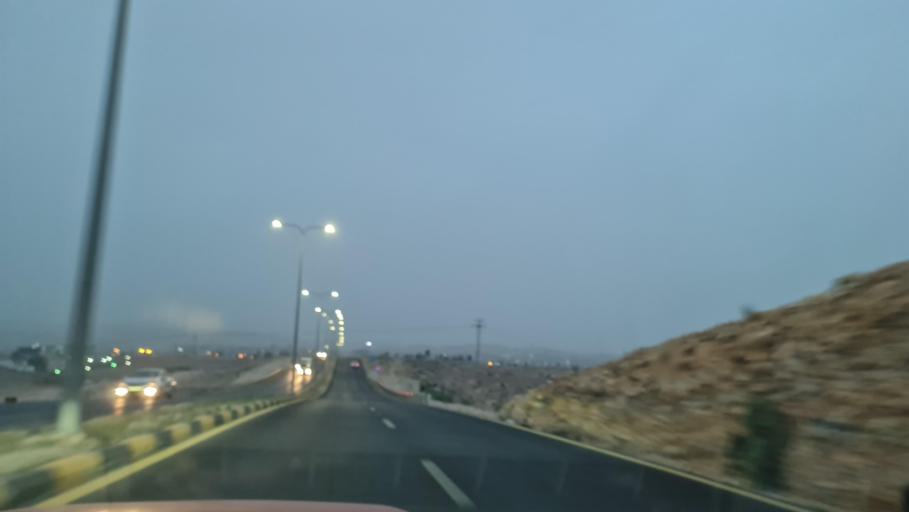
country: JO
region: Zarqa
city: Zarqa
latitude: 32.0485
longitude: 36.1049
